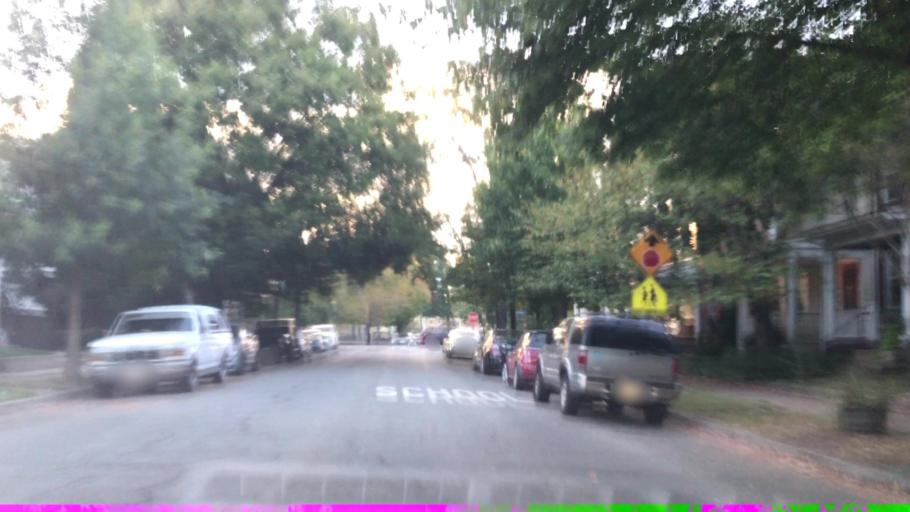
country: US
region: Virginia
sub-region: City of Richmond
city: Richmond
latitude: 37.5625
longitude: -77.4797
